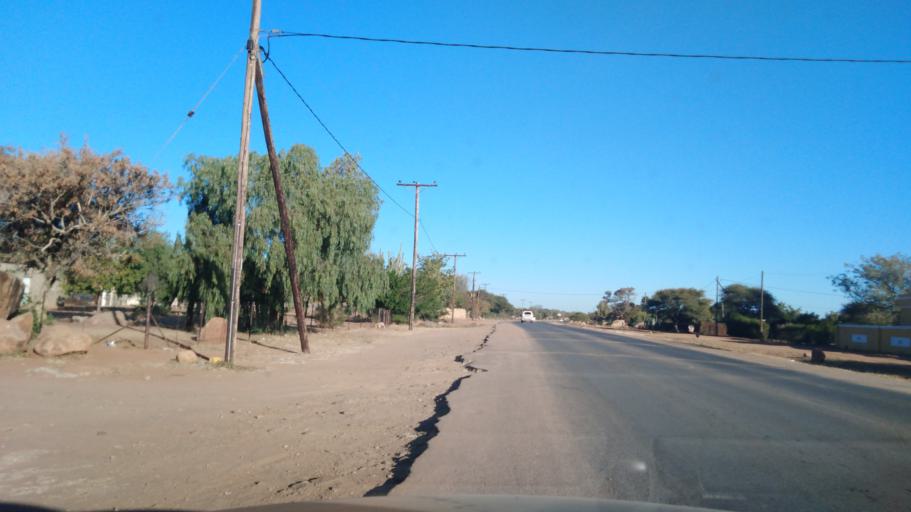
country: BW
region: Central
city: Mahalapye
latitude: -23.0876
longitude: 26.8249
